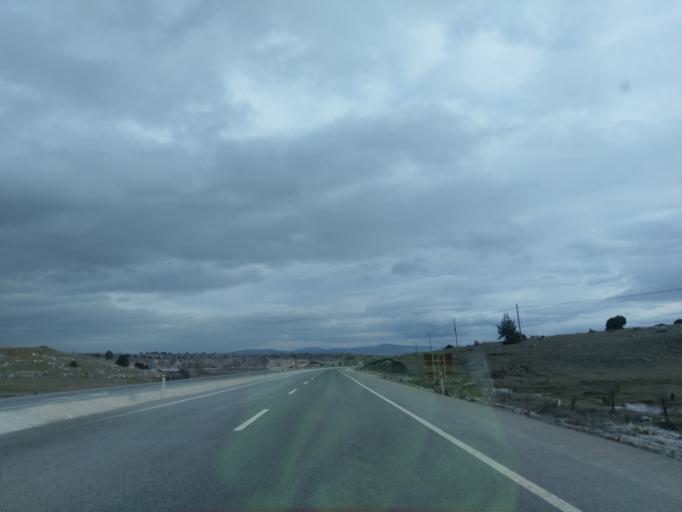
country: TR
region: Kuetahya
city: Aslanapa
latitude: 39.2314
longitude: 29.7717
